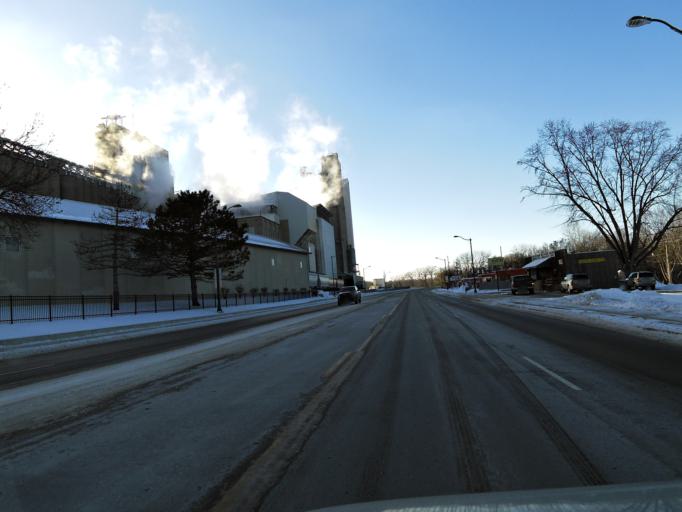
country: US
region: Minnesota
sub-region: Scott County
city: Shakopee
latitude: 44.7975
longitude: -93.5357
